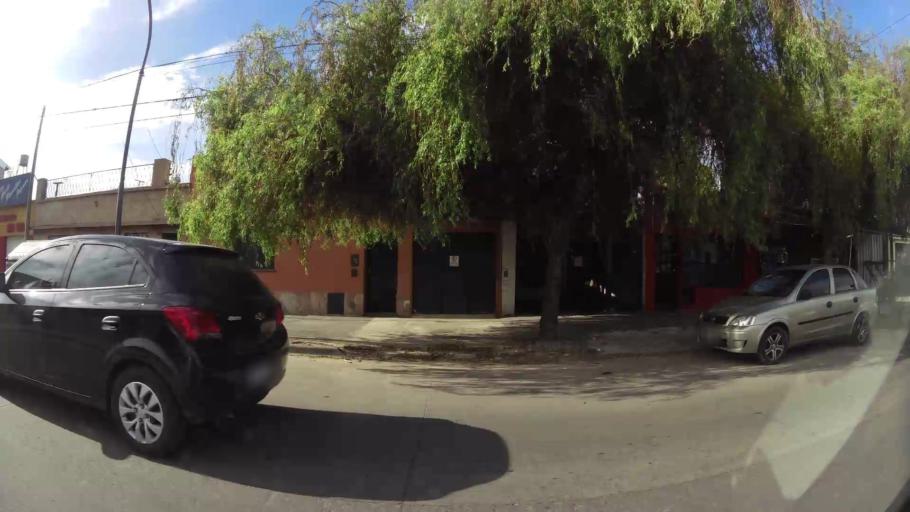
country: AR
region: Santa Fe
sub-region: Departamento de Rosario
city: Rosario
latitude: -32.9270
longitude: -60.6918
